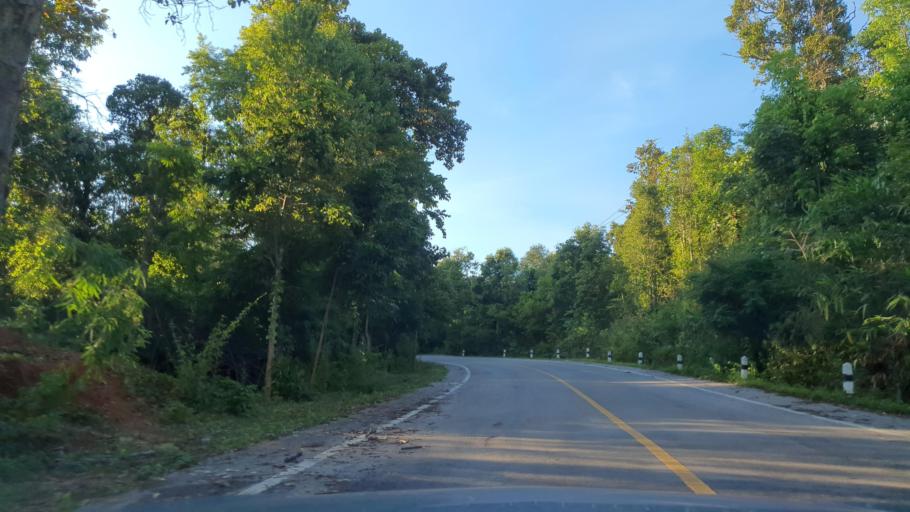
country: TH
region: Chiang Mai
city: Mae On
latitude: 18.8228
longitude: 99.2996
